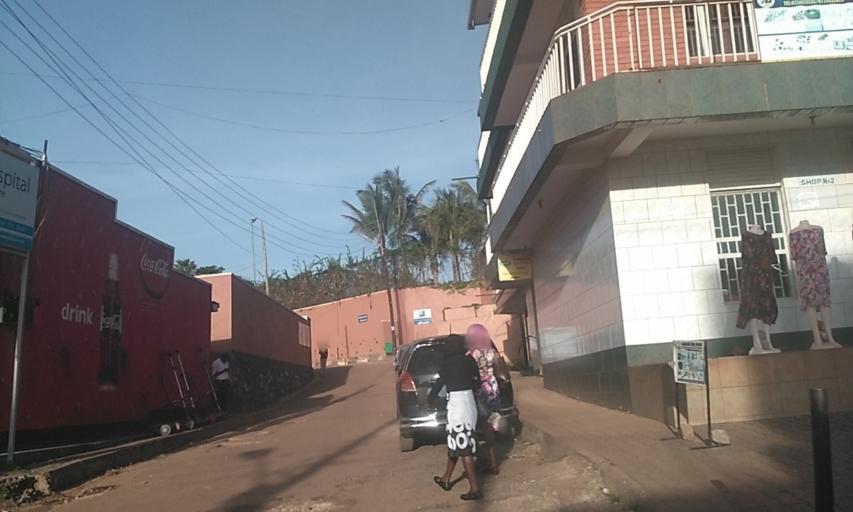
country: UG
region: Central Region
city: Kampala Central Division
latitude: 0.3500
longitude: 32.5985
